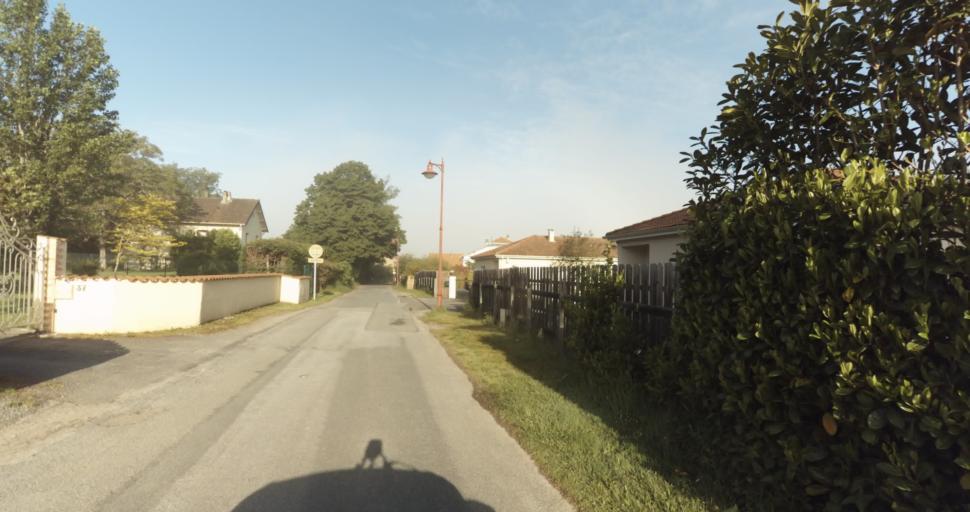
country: FR
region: Limousin
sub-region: Departement de la Haute-Vienne
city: Condat-sur-Vienne
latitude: 45.7825
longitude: 1.2820
